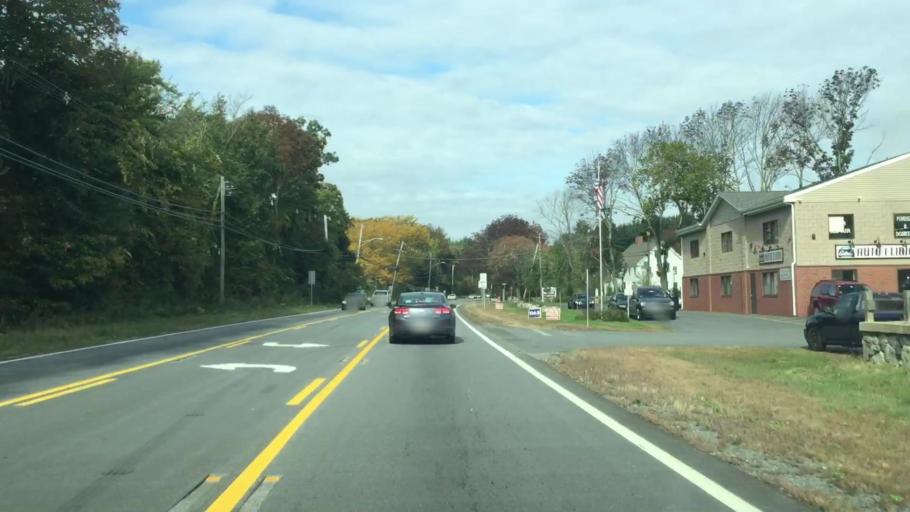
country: US
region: Massachusetts
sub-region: Middlesex County
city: North Reading
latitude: 42.6351
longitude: -71.0748
